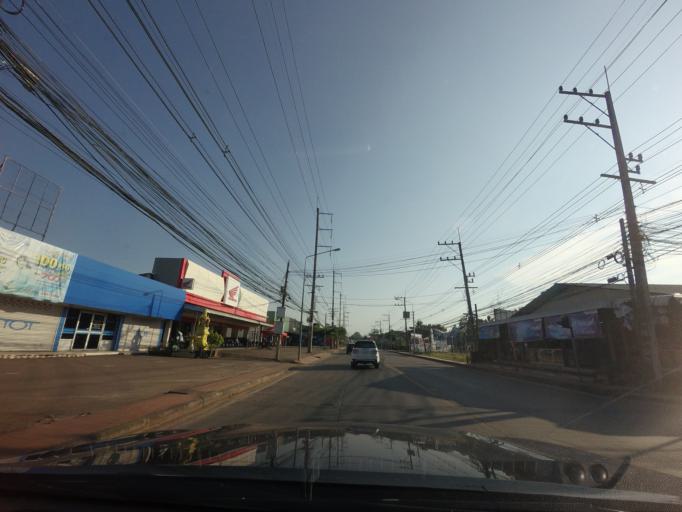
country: TH
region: Nan
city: Nan
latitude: 18.7739
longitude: 100.7655
